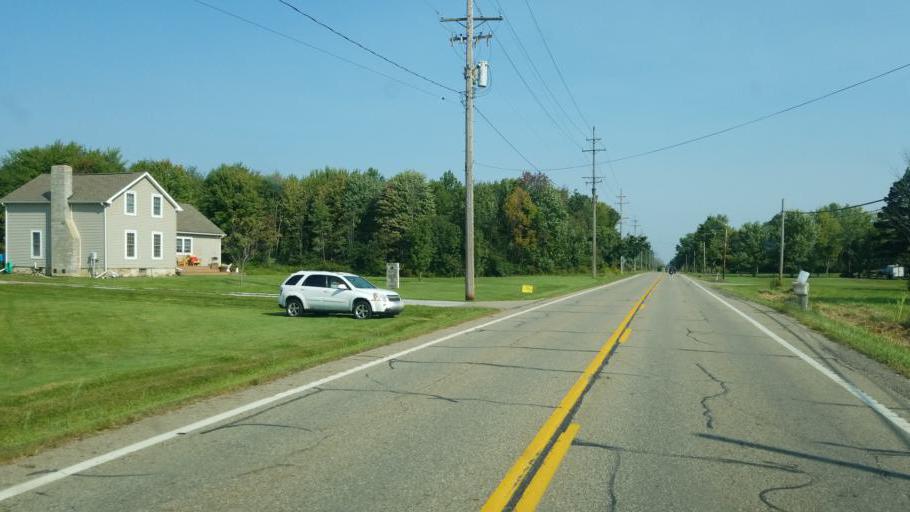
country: US
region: Ohio
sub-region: Ashtabula County
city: Orwell
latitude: 41.5775
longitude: -80.8651
